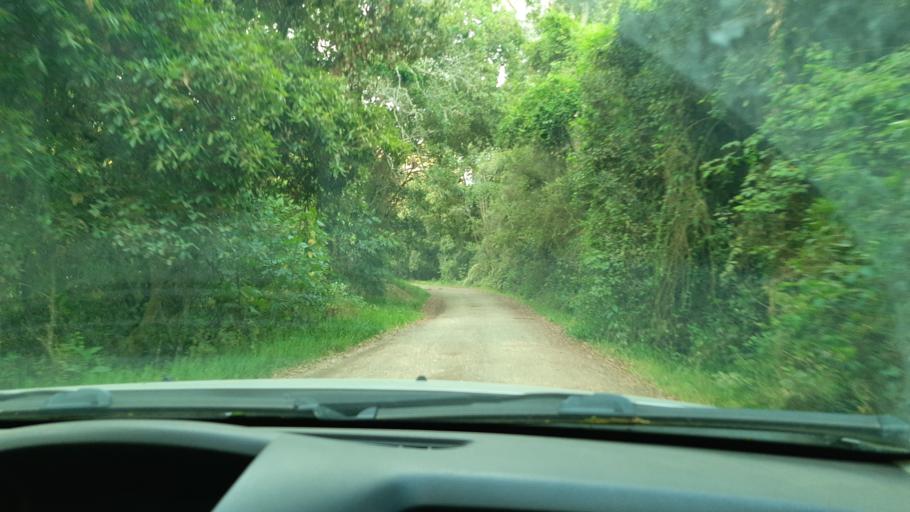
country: CO
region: Boyaca
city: La Capilla
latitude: 5.7134
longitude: -73.4777
